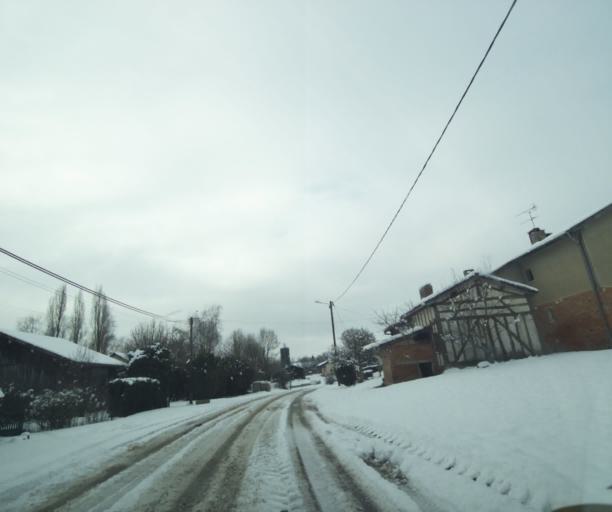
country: FR
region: Champagne-Ardenne
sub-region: Departement de la Haute-Marne
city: Montier-en-Der
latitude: 48.5179
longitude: 4.7003
